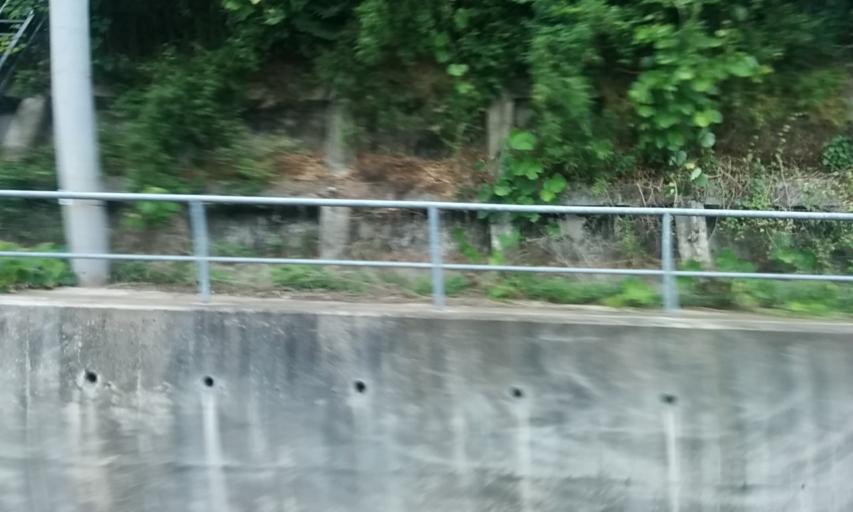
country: JP
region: Chiba
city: Sakura
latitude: 35.7392
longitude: 140.2004
